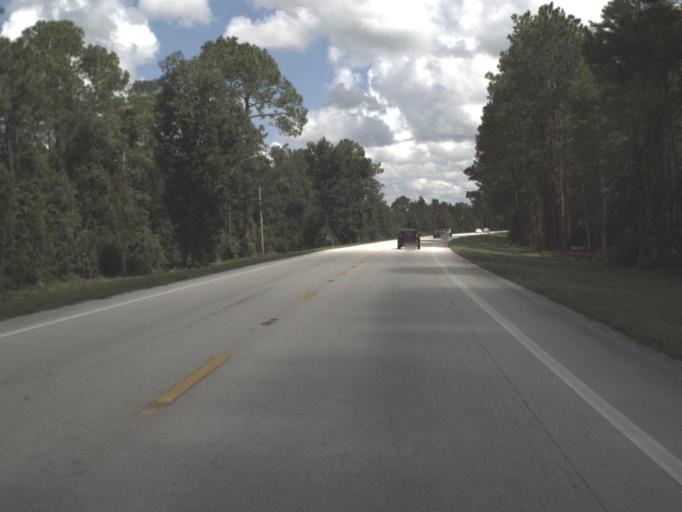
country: US
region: Florida
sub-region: Polk County
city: Polk City
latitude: 28.3328
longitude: -81.8331
